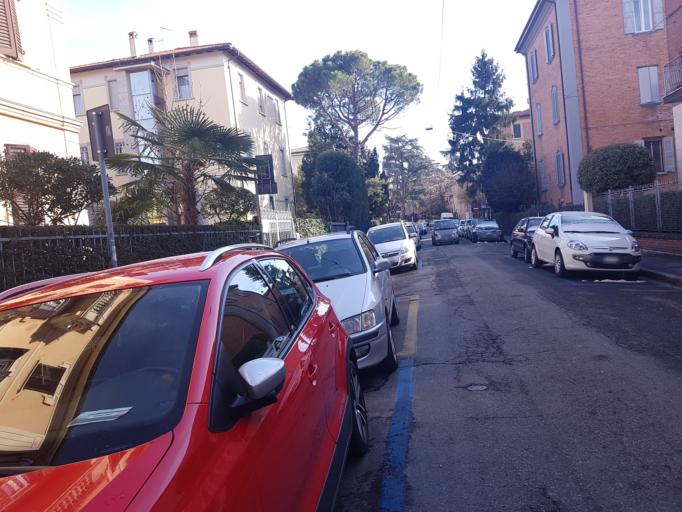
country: IT
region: Emilia-Romagna
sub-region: Provincia di Bologna
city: Bologna
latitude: 44.4937
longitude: 11.3222
